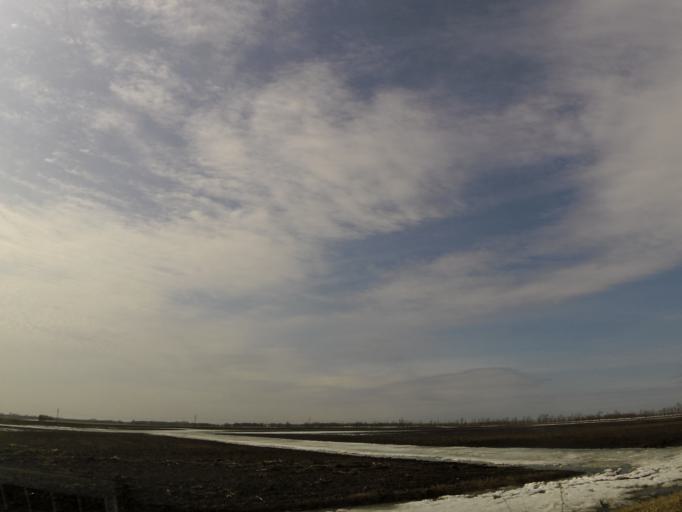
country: US
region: North Dakota
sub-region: Walsh County
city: Grafton
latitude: 48.4305
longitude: -97.2559
